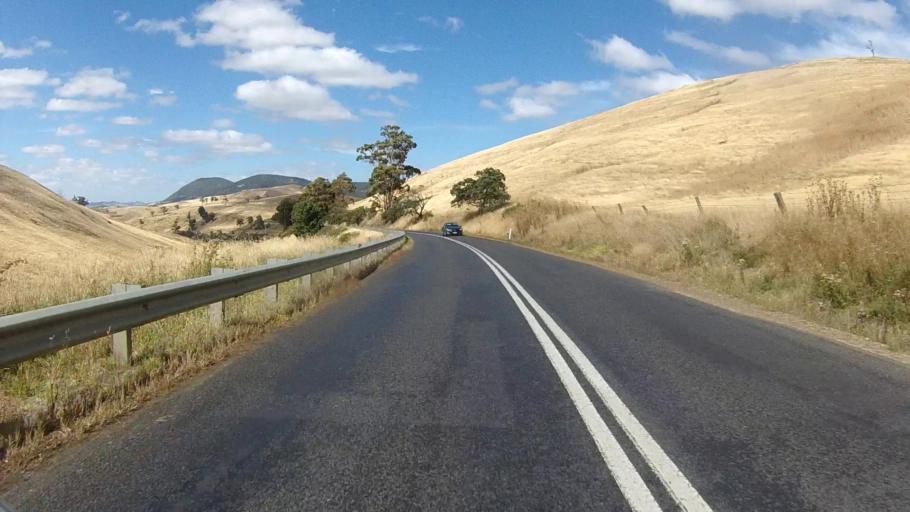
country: AU
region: Tasmania
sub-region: Brighton
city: Bridgewater
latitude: -42.5614
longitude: 147.3912
